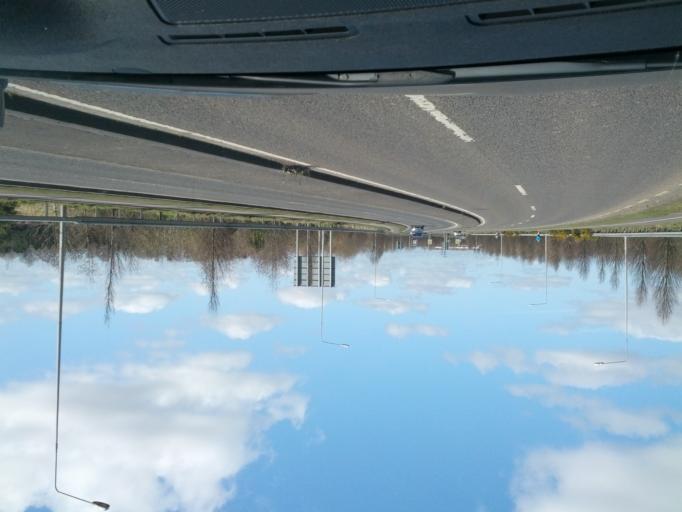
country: IE
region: Leinster
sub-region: Kildare
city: Celbridge
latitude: 53.3619
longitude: -6.5313
